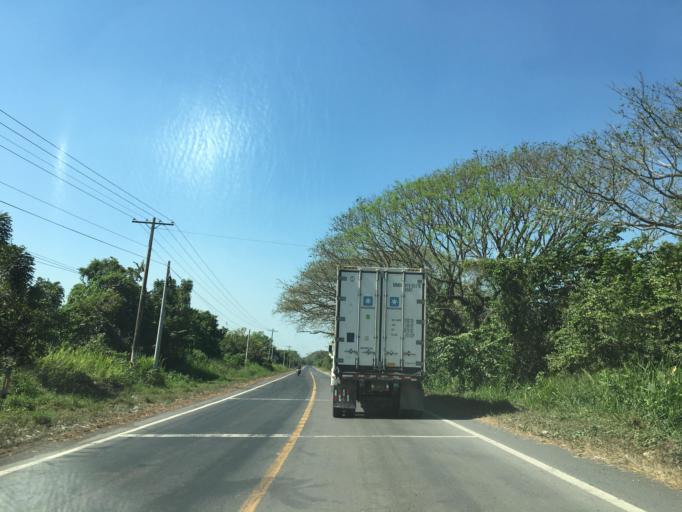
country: GT
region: Escuintla
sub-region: Municipio de Masagua
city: Masagua
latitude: 14.1816
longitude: -90.8659
